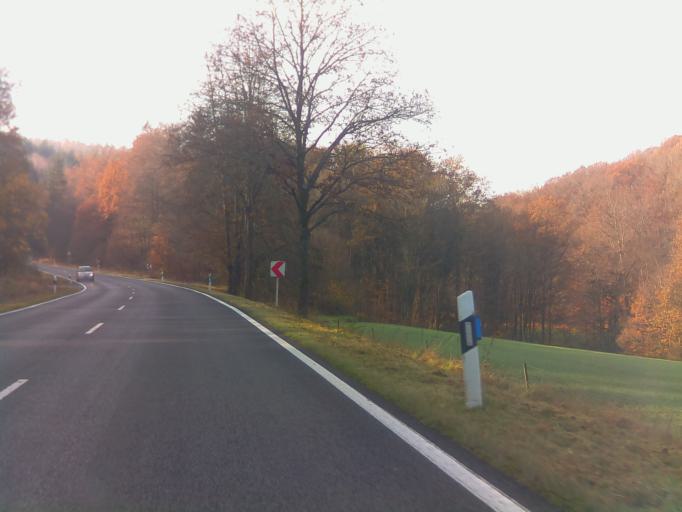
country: DE
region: Bavaria
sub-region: Regierungsbezirk Unterfranken
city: Bad Bocklet
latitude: 50.2534
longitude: 10.0427
